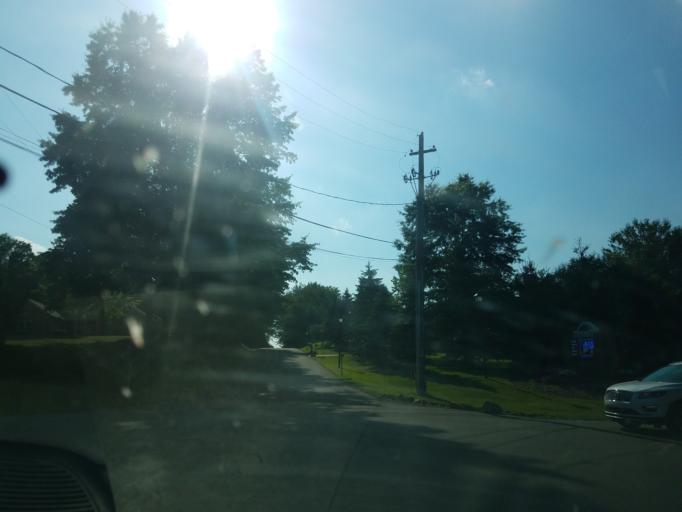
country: US
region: Ohio
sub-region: Summit County
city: Greensburg
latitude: 40.9509
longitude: -81.4372
